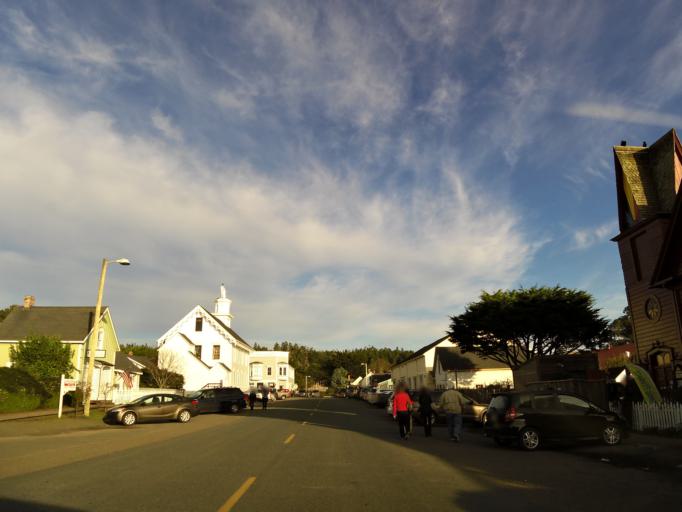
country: US
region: California
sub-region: Mendocino County
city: Fort Bragg
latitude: 39.3061
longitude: -123.7997
